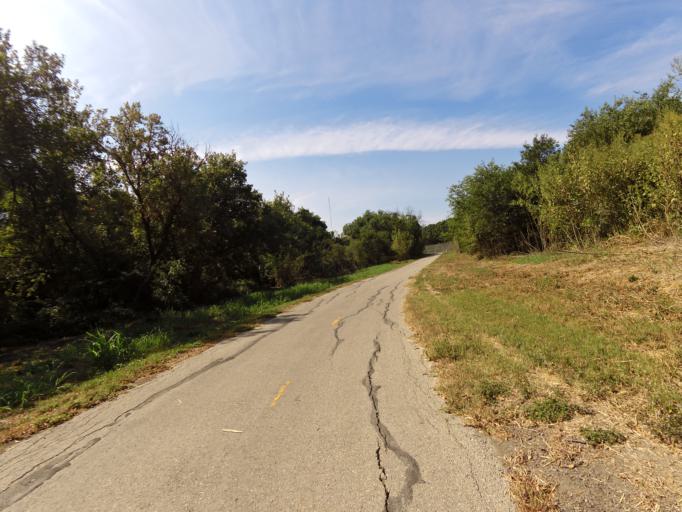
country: US
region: Texas
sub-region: Bexar County
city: Terrell Hills
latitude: 29.4275
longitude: -98.4262
